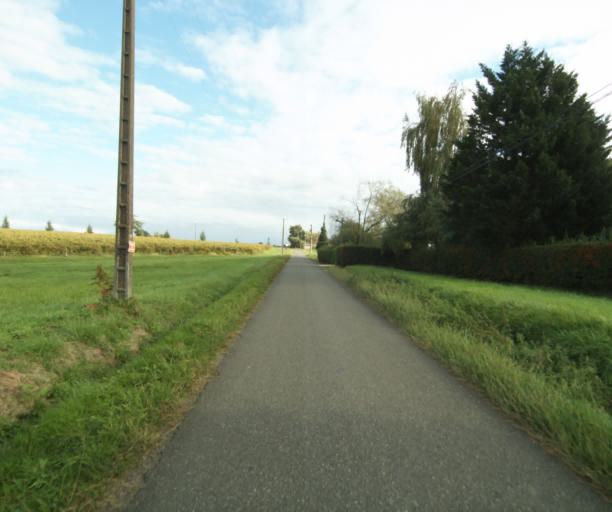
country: FR
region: Midi-Pyrenees
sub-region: Departement du Gers
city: Eauze
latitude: 43.8843
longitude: 0.0745
